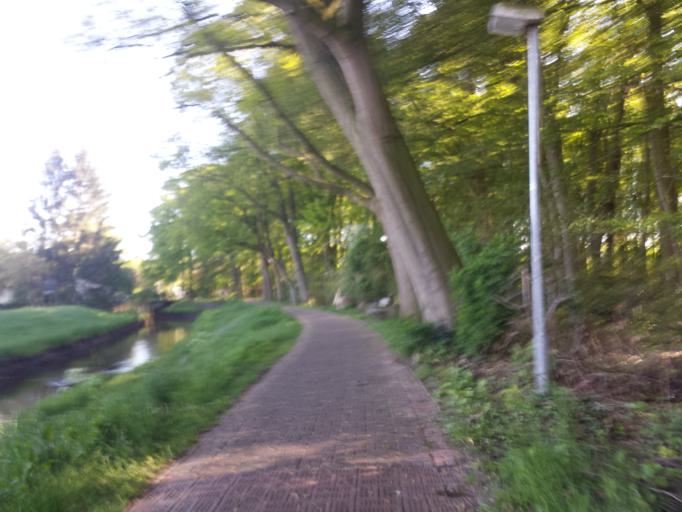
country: DE
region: Lower Saxony
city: Lilienthal
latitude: 53.1447
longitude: 8.9142
